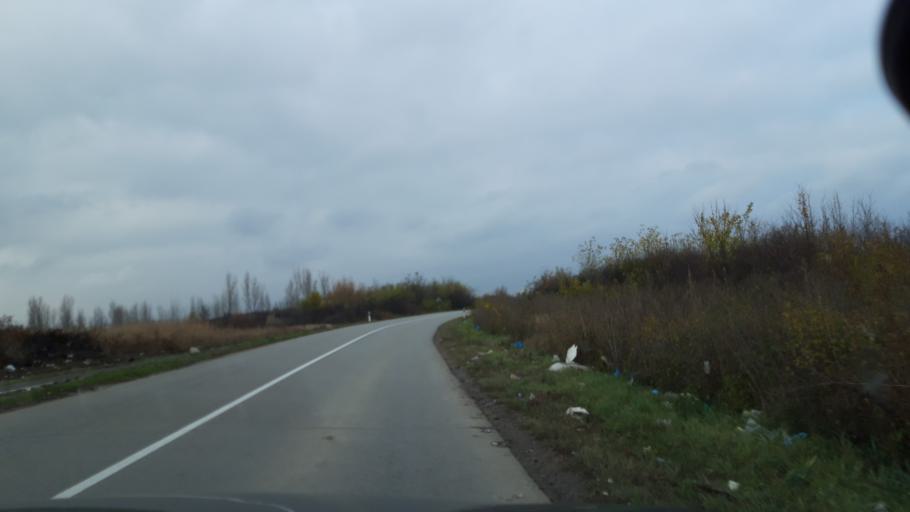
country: RS
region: Autonomna Pokrajina Vojvodina
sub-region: Severnobanatski Okrug
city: Novi Knezevac
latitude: 46.0758
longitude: 20.1033
